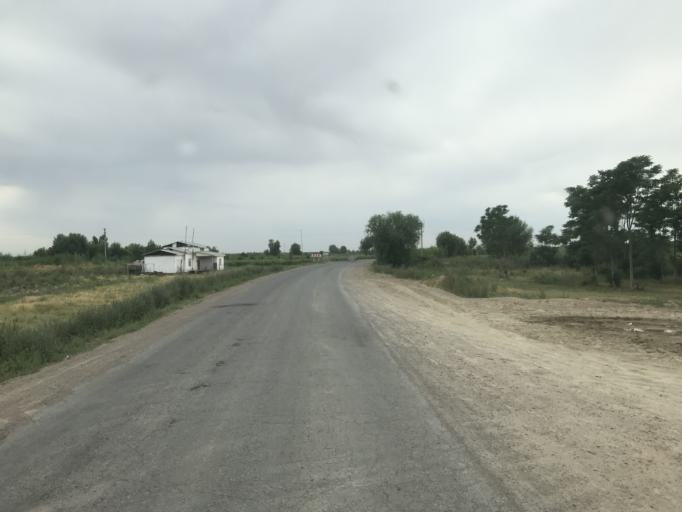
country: KZ
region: Ongtustik Qazaqstan
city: Asykata
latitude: 40.9548
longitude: 68.4624
